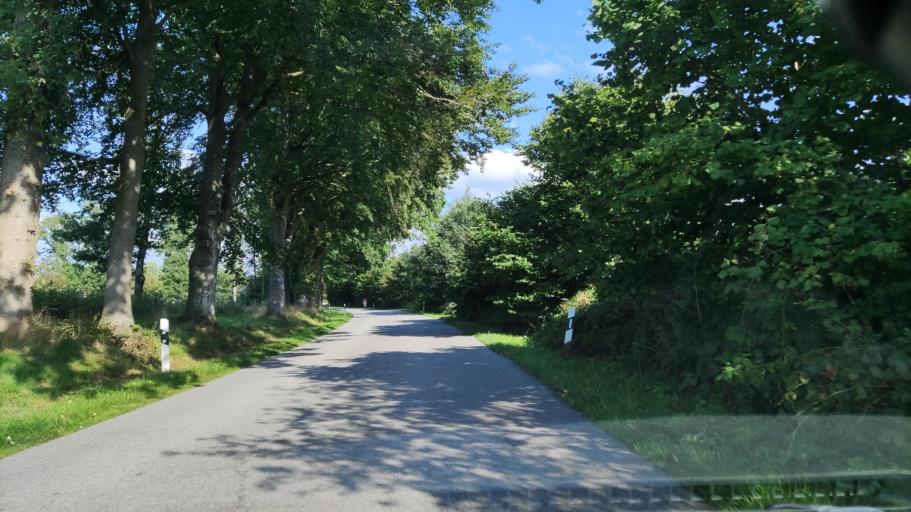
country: DE
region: Schleswig-Holstein
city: Aukrug
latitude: 54.0773
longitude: 9.7709
